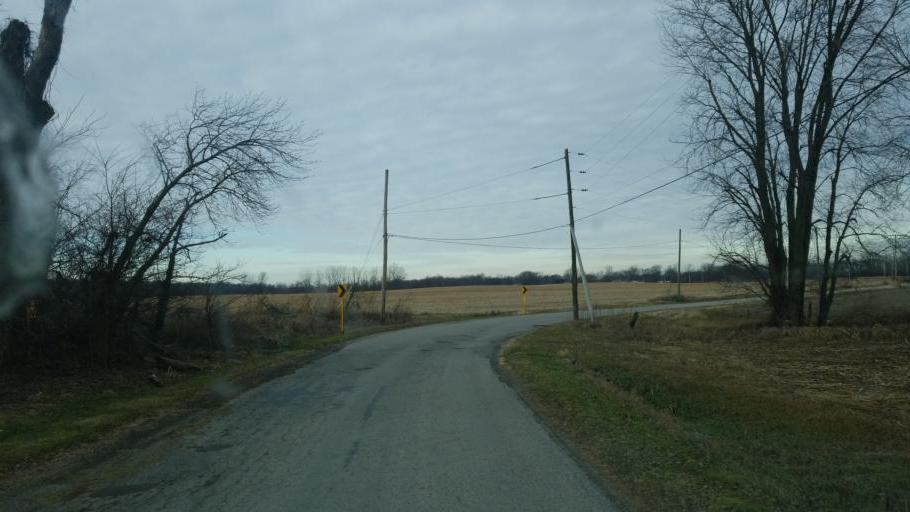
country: US
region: Ohio
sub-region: Morrow County
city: Mount Gilead
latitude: 40.6291
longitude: -82.8678
